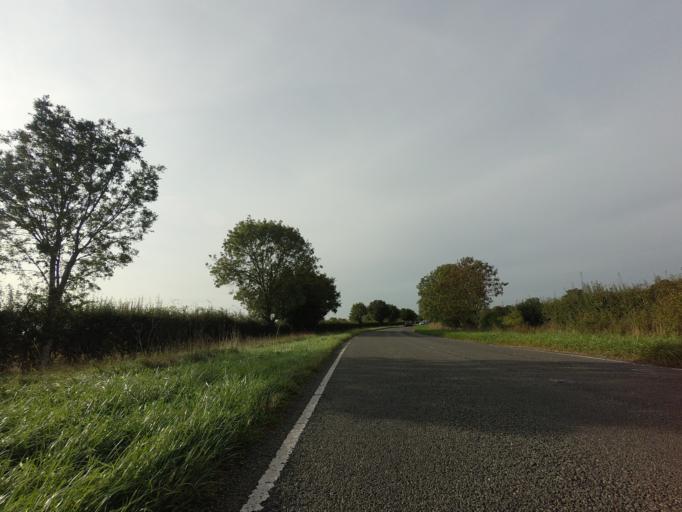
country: GB
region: England
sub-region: Cambridgeshire
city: Harston
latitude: 52.0982
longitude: 0.0820
